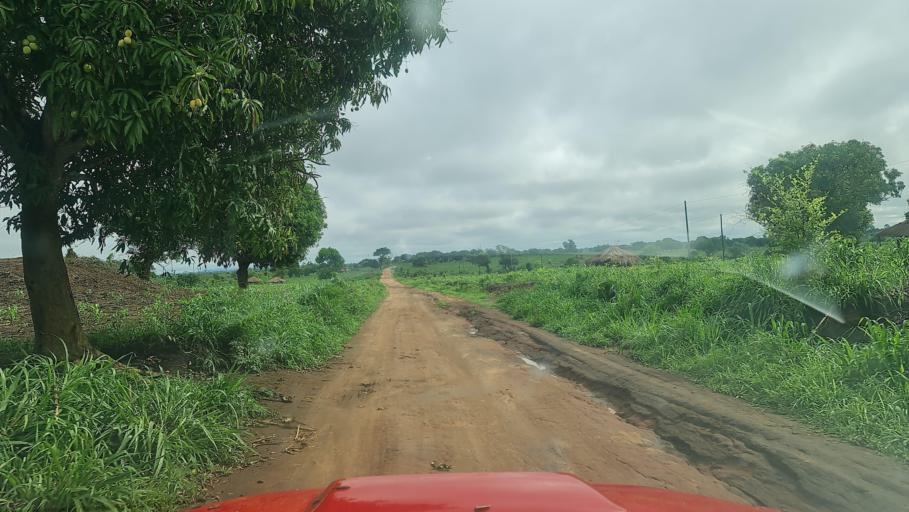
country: MW
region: Southern Region
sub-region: Nsanje District
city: Nsanje
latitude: -17.2090
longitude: 35.6798
